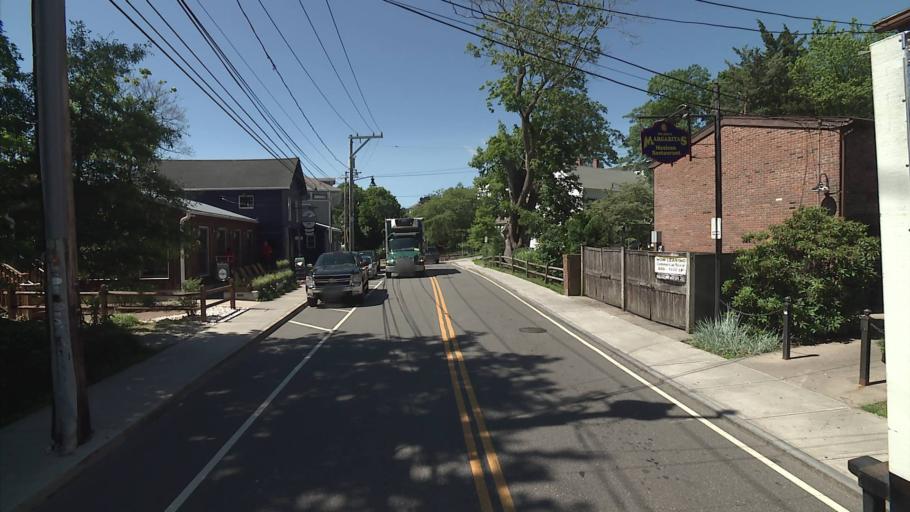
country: US
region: Connecticut
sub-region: New London County
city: Mystic
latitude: 41.3531
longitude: -71.9720
